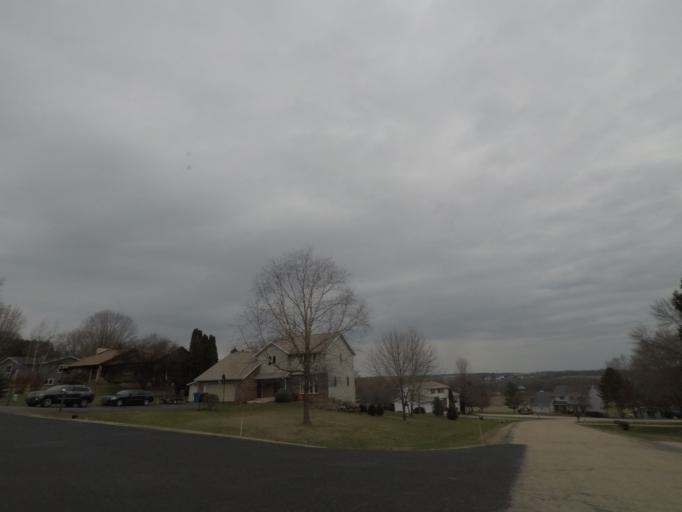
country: US
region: Wisconsin
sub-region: Dane County
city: Middleton
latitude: 43.1057
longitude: -89.5529
